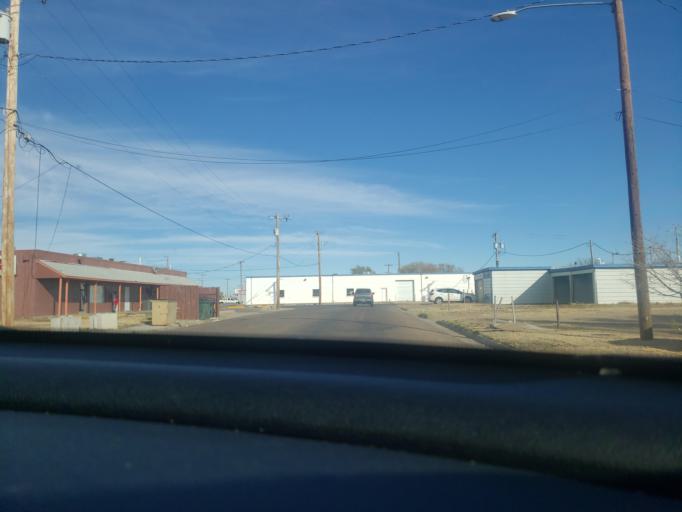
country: US
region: Kansas
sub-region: Finney County
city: Garden City
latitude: 37.9759
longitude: -100.8825
